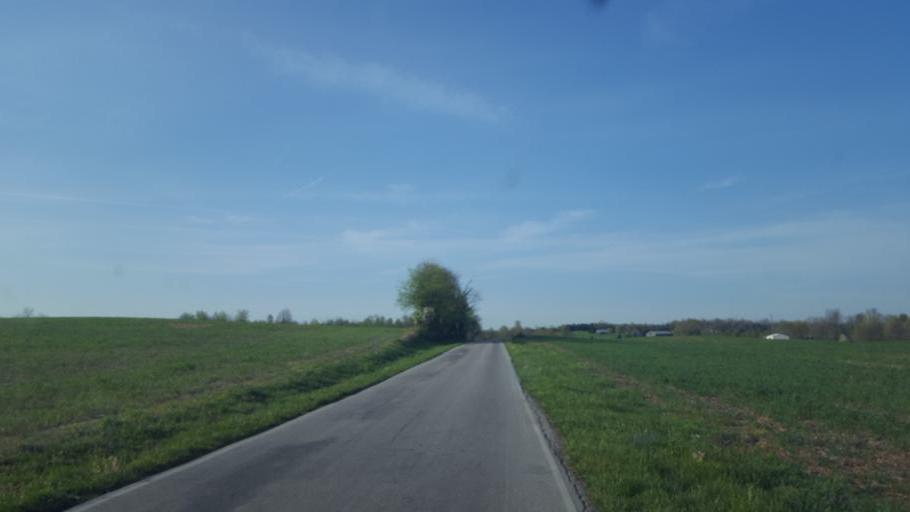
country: US
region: Kentucky
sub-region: Hardin County
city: Elizabethtown
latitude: 37.4953
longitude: -85.9610
